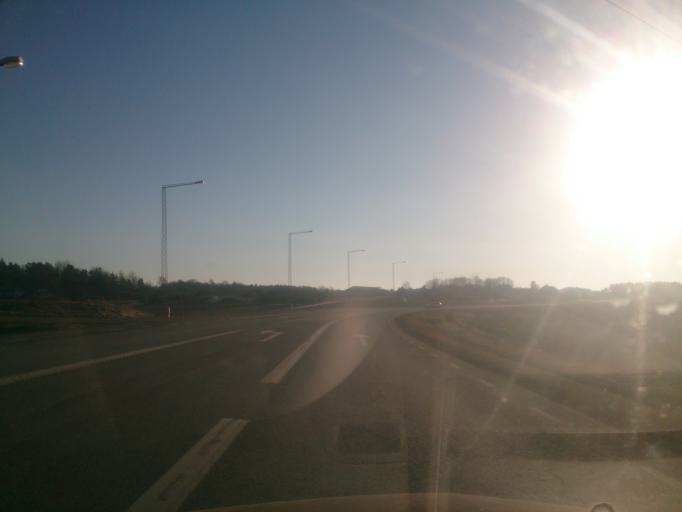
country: SE
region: OEstergoetland
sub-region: Norrkopings Kommun
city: Kimstad
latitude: 58.4892
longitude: 15.9488
